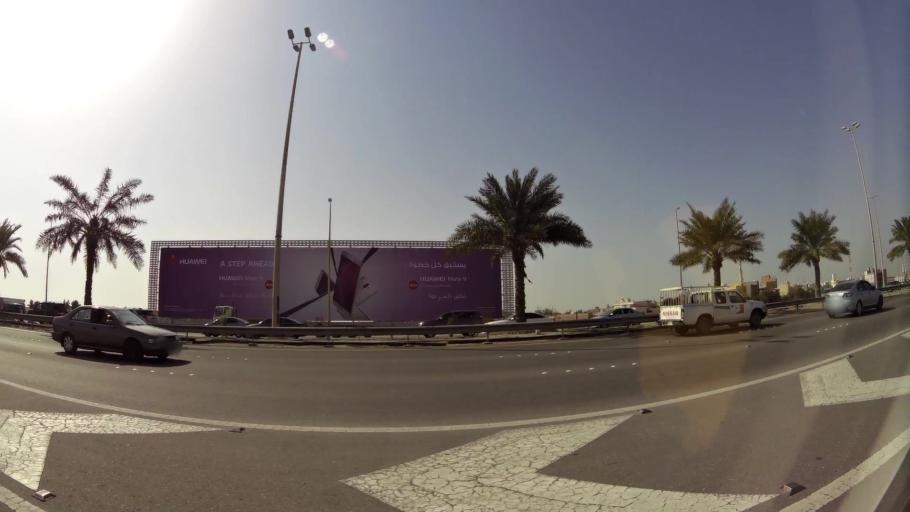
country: BH
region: Manama
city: Jidd Hafs
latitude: 26.2127
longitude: 50.5196
